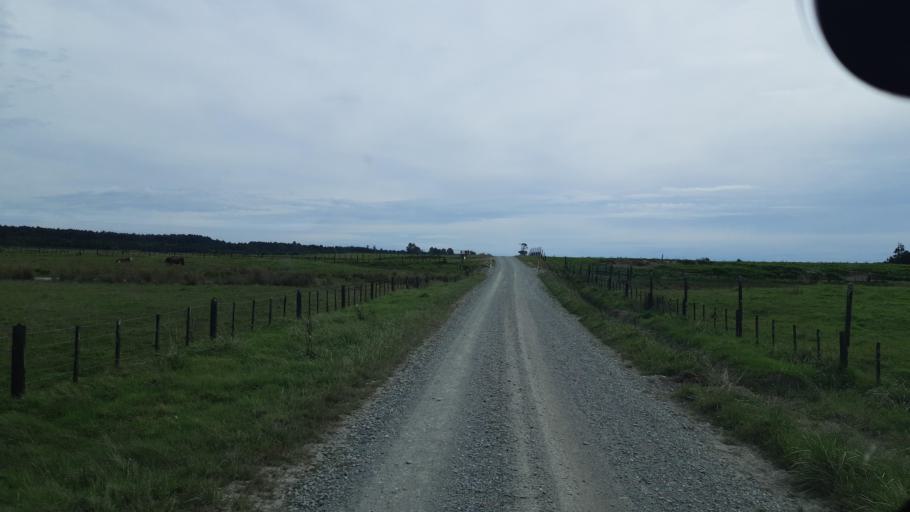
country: NZ
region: West Coast
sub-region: Westland District
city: Hokitika
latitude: -42.9716
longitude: 170.6757
